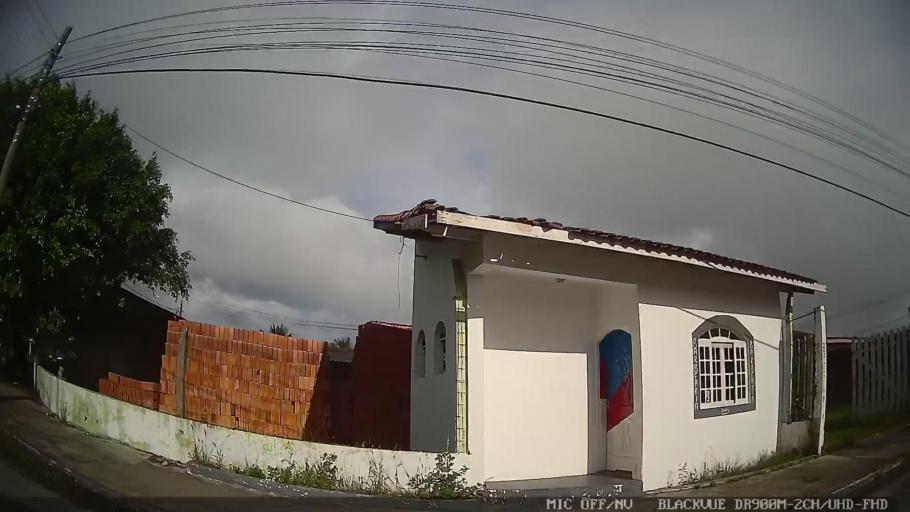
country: BR
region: Sao Paulo
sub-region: Itanhaem
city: Itanhaem
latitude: -24.2290
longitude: -46.8720
